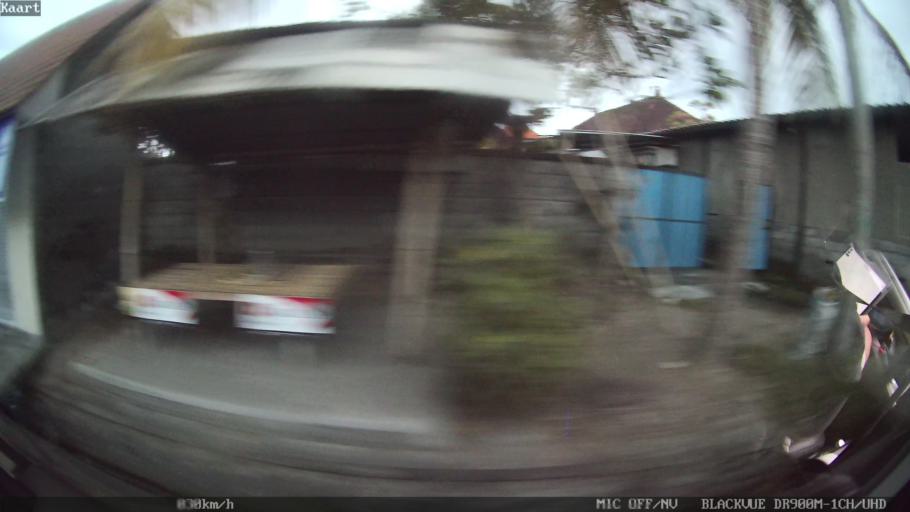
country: ID
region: Bali
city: Banjar Pasekan
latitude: -8.6180
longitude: 115.2977
